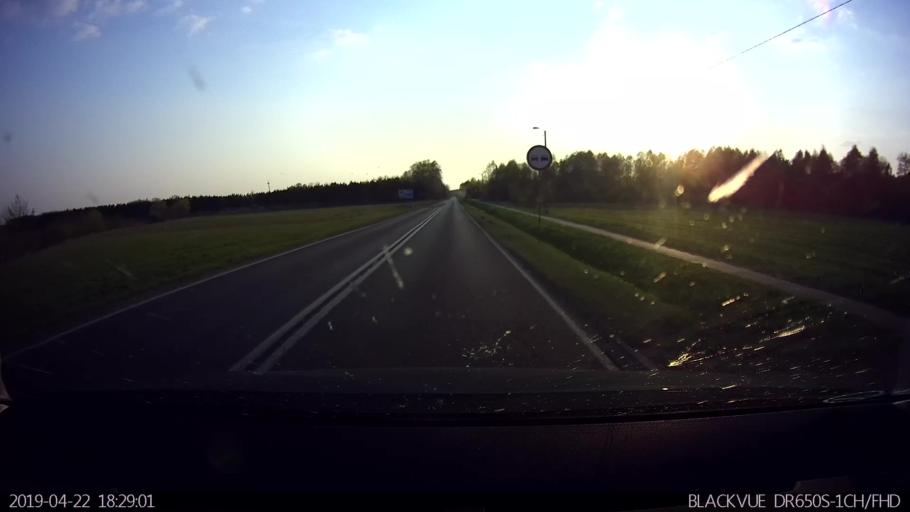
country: PL
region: Masovian Voivodeship
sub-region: Powiat wolominski
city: Tluszcz
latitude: 52.4550
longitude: 21.4614
